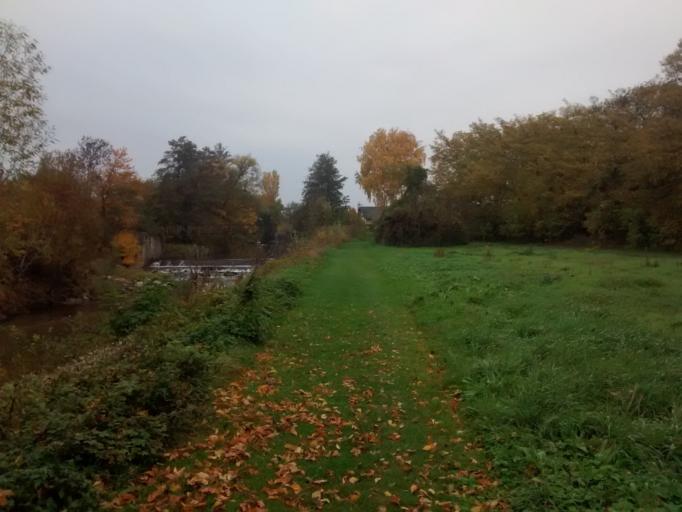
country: AT
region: Lower Austria
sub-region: Politischer Bezirk Modling
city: Munchendorf
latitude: 48.0156
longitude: 16.3685
